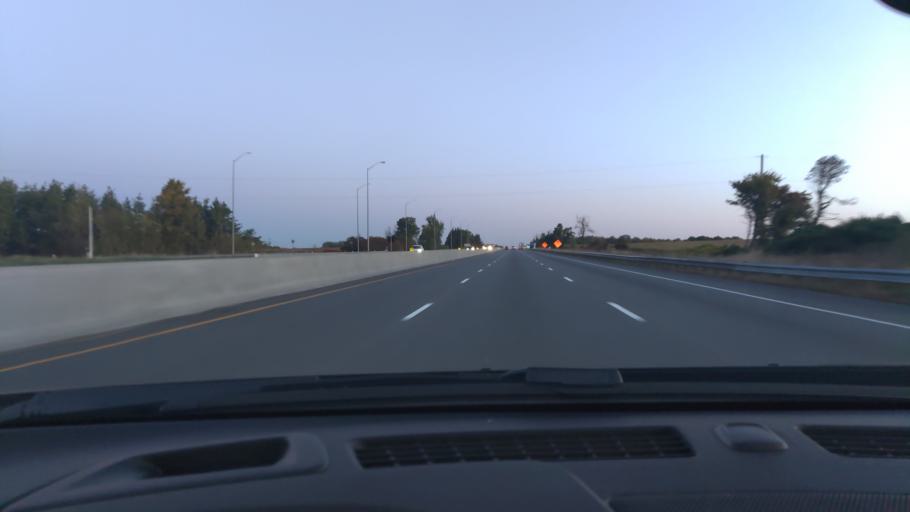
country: CA
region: Ontario
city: Innisfil
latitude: 44.2478
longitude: -79.6697
